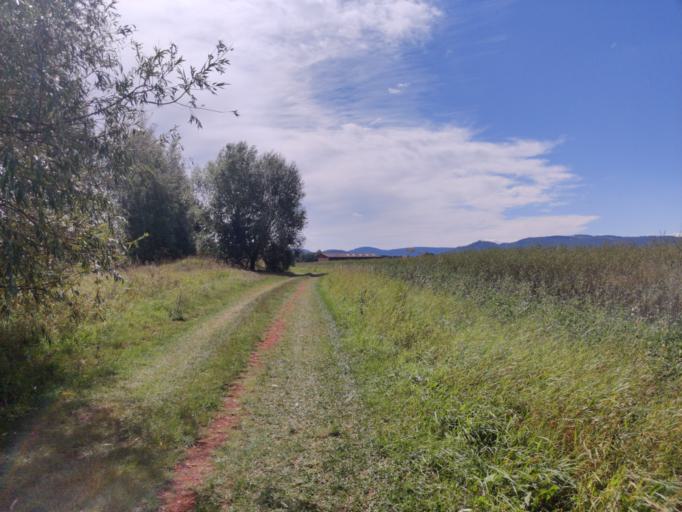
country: DE
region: Lower Saxony
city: Langelsheim
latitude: 51.9741
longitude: 10.3701
